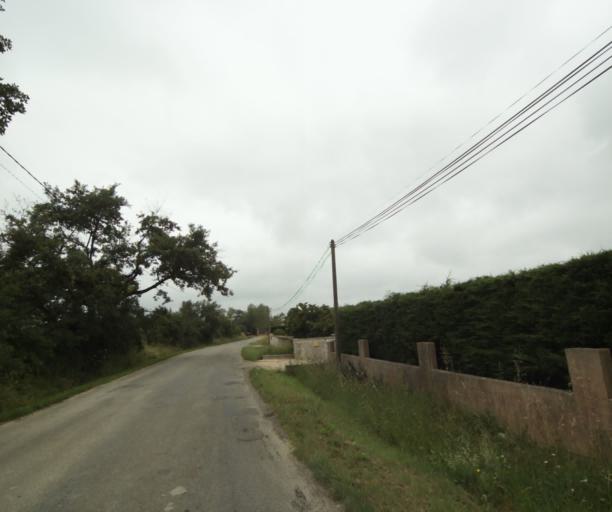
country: FR
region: Midi-Pyrenees
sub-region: Departement du Tarn-et-Garonne
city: Montbeton
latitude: 43.9905
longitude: 1.3067
